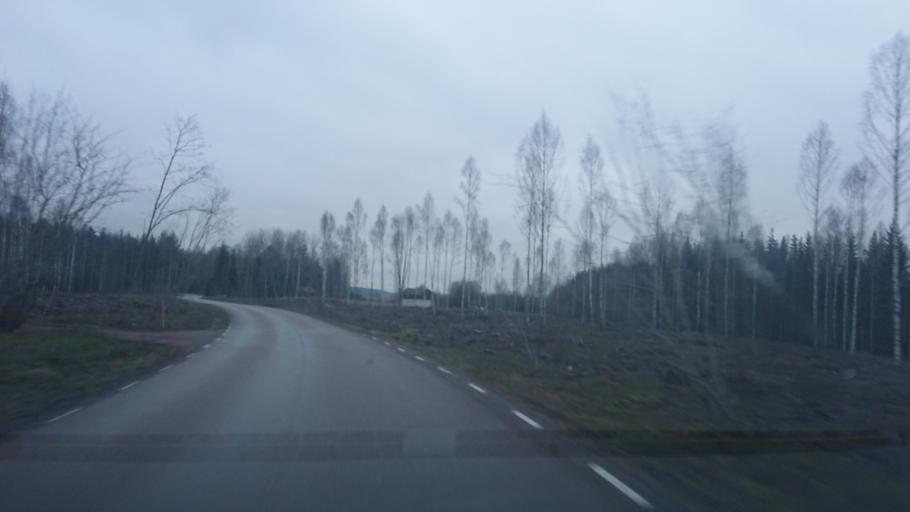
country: SE
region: Uppsala
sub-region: Osthammars Kommun
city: Bjorklinge
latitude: 60.0231
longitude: 17.5742
